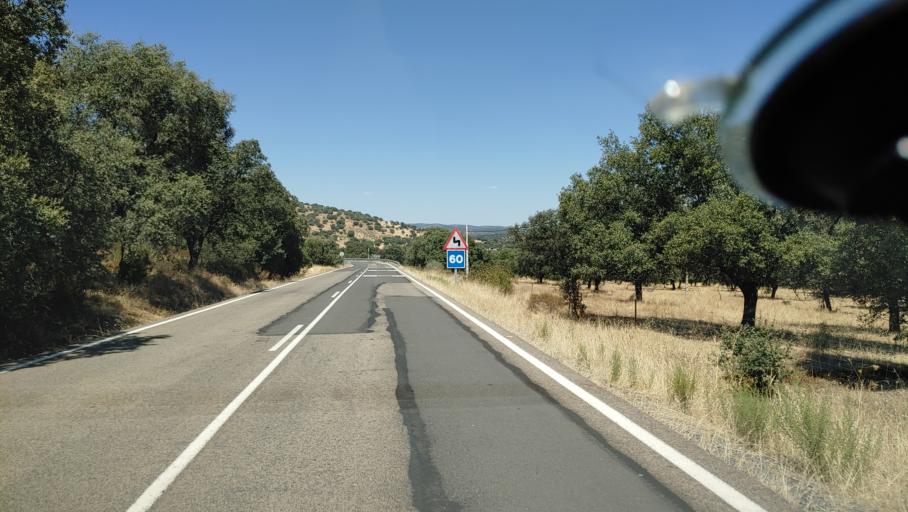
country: ES
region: Castille-La Mancha
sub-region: Provincia de Ciudad Real
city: Alamillo
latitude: 38.7510
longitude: -4.6999
